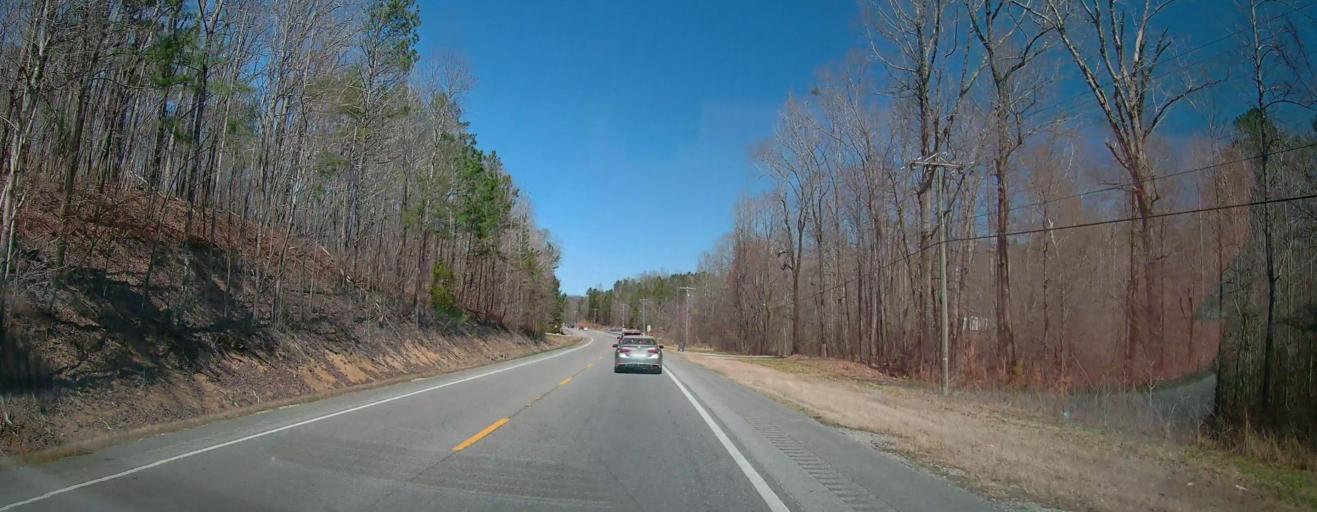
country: US
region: Alabama
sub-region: Calhoun County
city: Ohatchee
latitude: 33.8086
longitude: -86.0362
